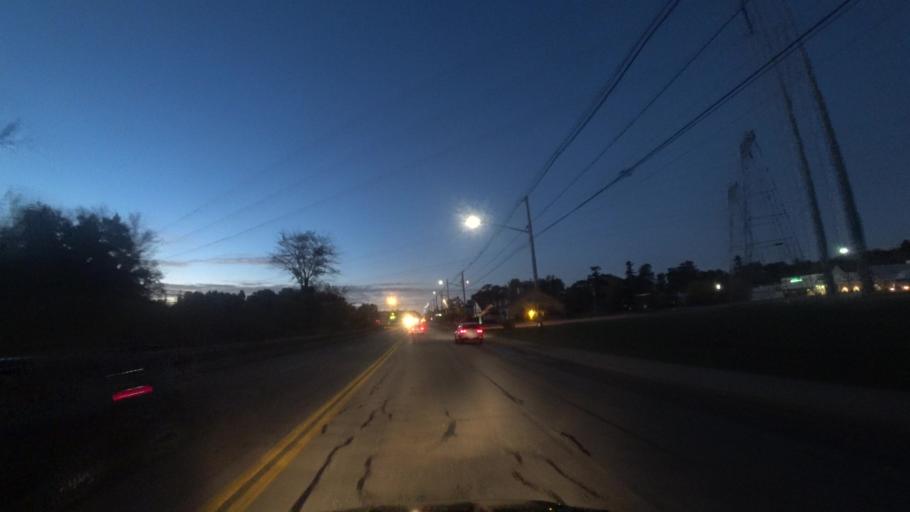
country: US
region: Massachusetts
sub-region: Middlesex County
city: North Reading
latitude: 42.5719
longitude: -71.1099
